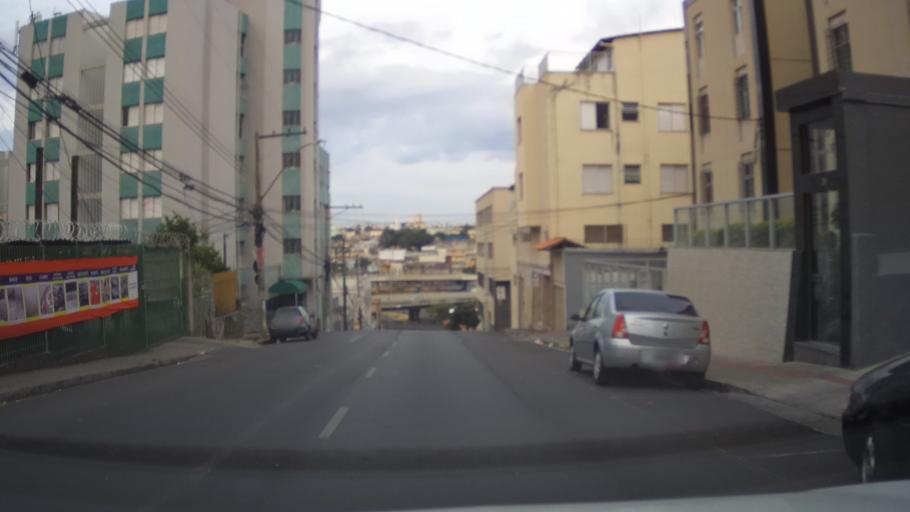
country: BR
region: Minas Gerais
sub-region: Belo Horizonte
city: Belo Horizonte
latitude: -19.9115
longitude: -43.9371
